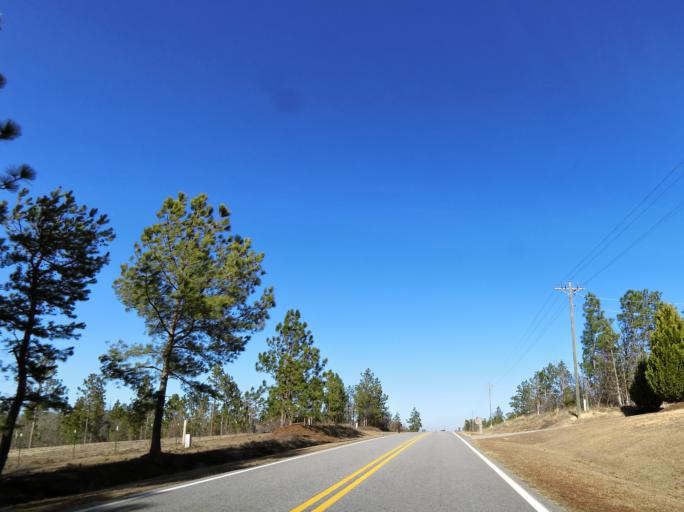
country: US
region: Georgia
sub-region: Crawford County
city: Knoxville
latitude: 32.7456
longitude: -83.9015
